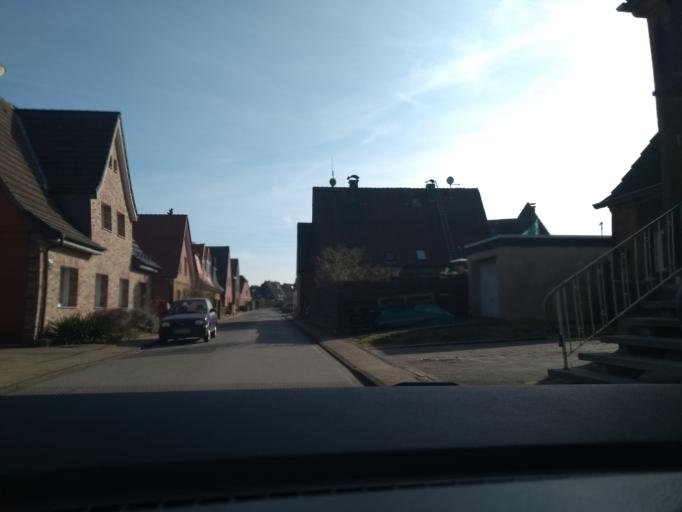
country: DE
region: North Rhine-Westphalia
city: Selm
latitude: 51.6959
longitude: 7.4577
